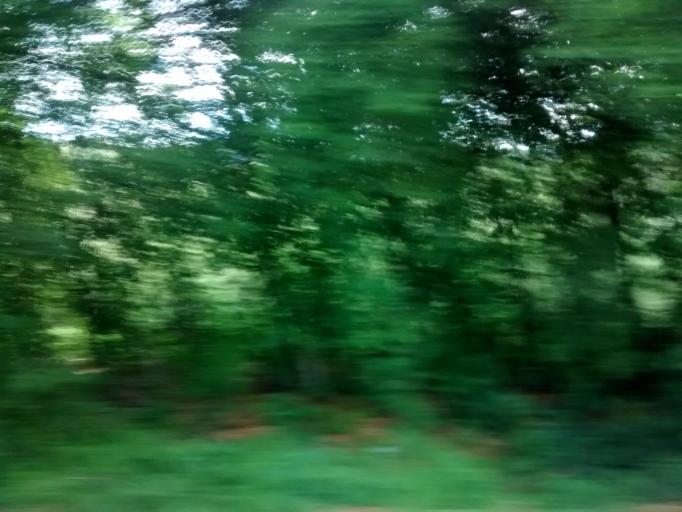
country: CO
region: Cundinamarca
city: Ricaurte
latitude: 4.2457
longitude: -74.7232
